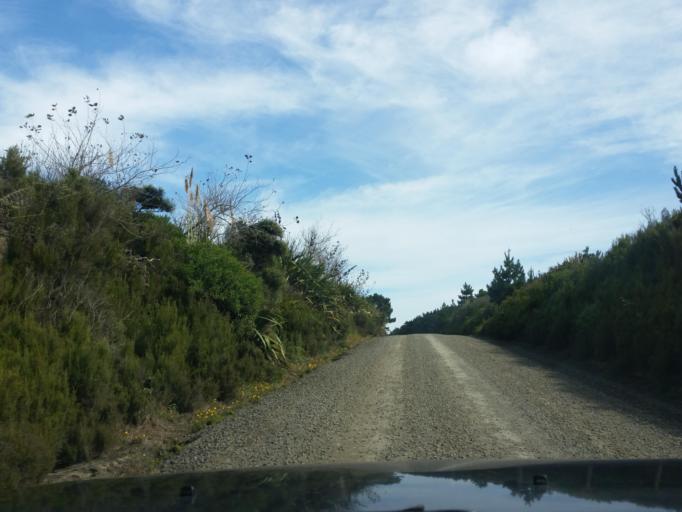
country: NZ
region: Northland
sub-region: Kaipara District
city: Dargaville
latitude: -35.9318
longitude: 173.7582
